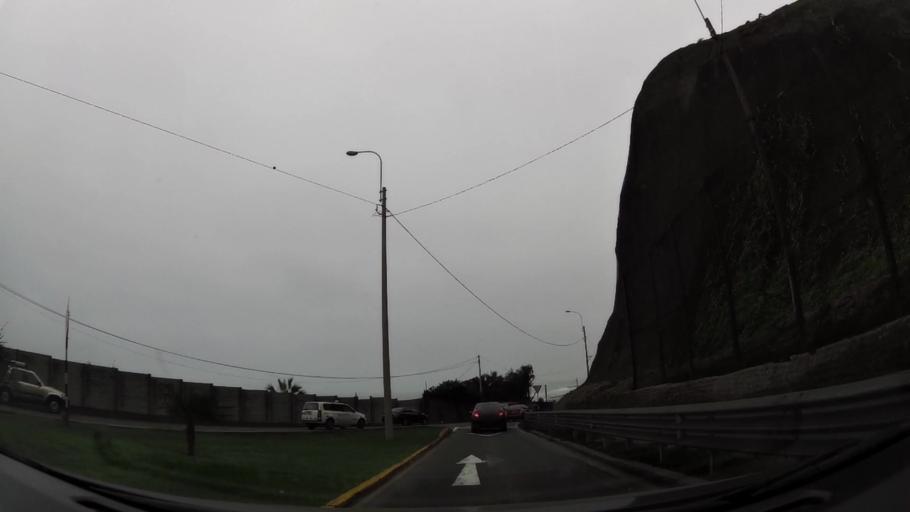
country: PE
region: Lima
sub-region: Lima
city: San Isidro
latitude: -12.1266
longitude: -77.0375
